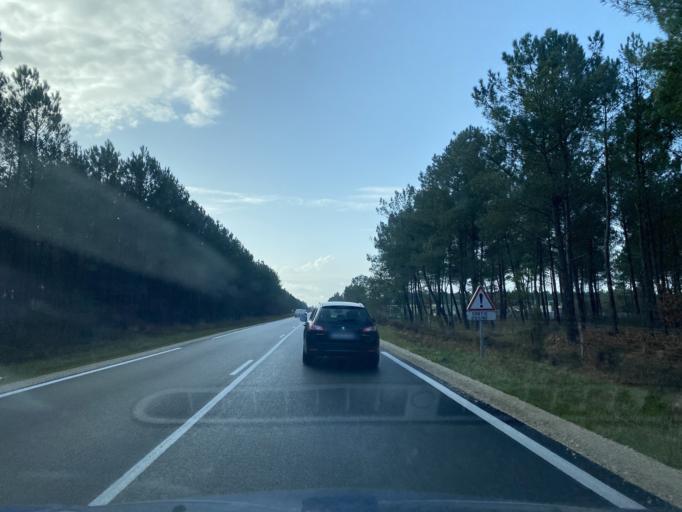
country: FR
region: Aquitaine
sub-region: Departement de la Gironde
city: Martignas-sur-Jalle
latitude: 44.8155
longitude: -0.8553
